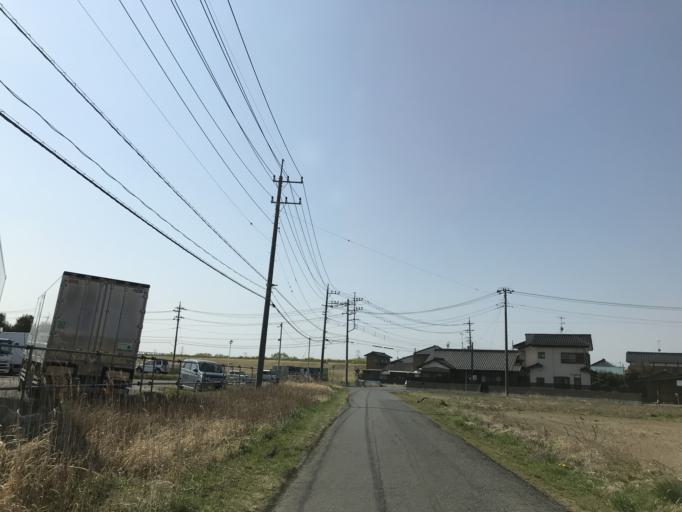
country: JP
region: Ibaraki
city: Moriya
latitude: 35.9376
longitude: 139.9594
